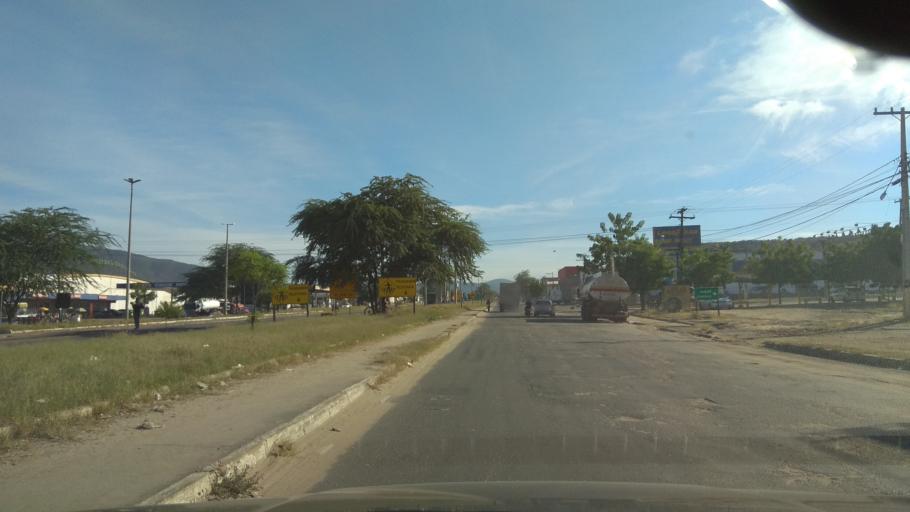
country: BR
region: Bahia
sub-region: Jequie
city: Jequie
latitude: -13.8583
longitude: -40.1133
